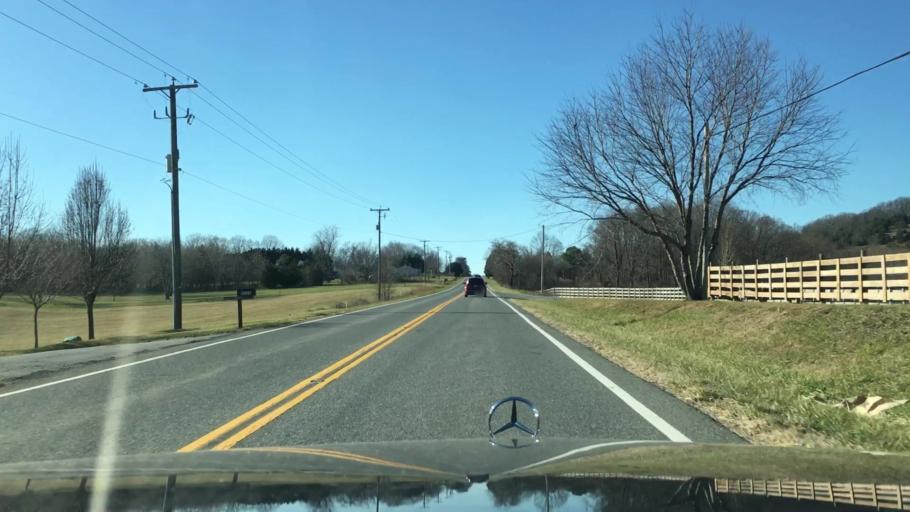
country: US
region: Virginia
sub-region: City of Bedford
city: Bedford
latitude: 37.2396
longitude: -79.6469
